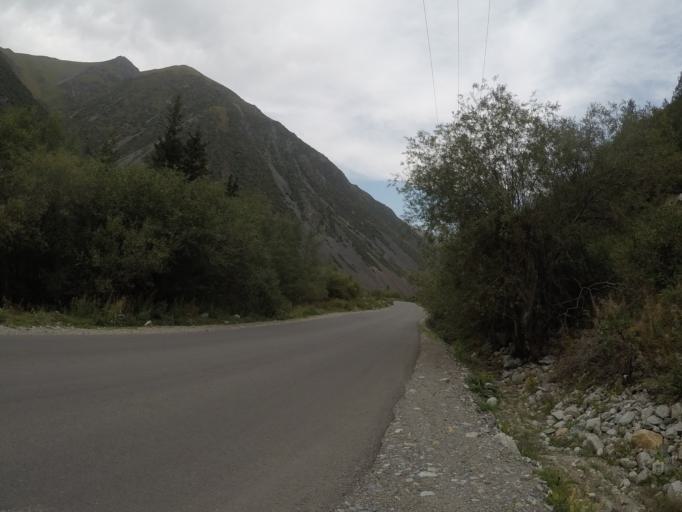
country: KG
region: Chuy
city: Bishkek
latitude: 42.5741
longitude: 74.4829
